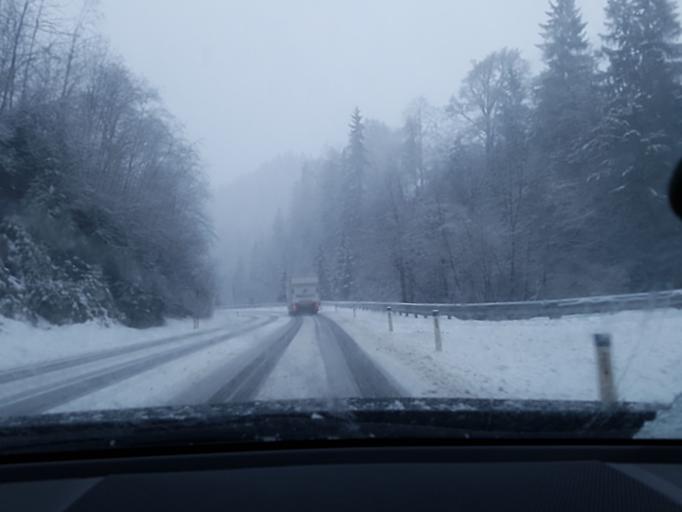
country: AT
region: Salzburg
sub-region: Politischer Bezirk Hallein
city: Abtenau
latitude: 47.5947
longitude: 13.3033
